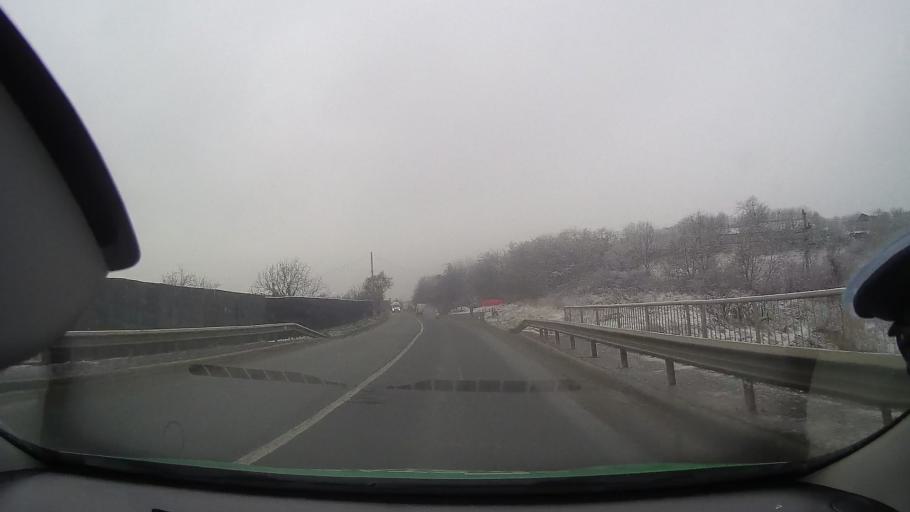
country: RO
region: Cluj
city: Turda
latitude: 46.5633
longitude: 23.7754
